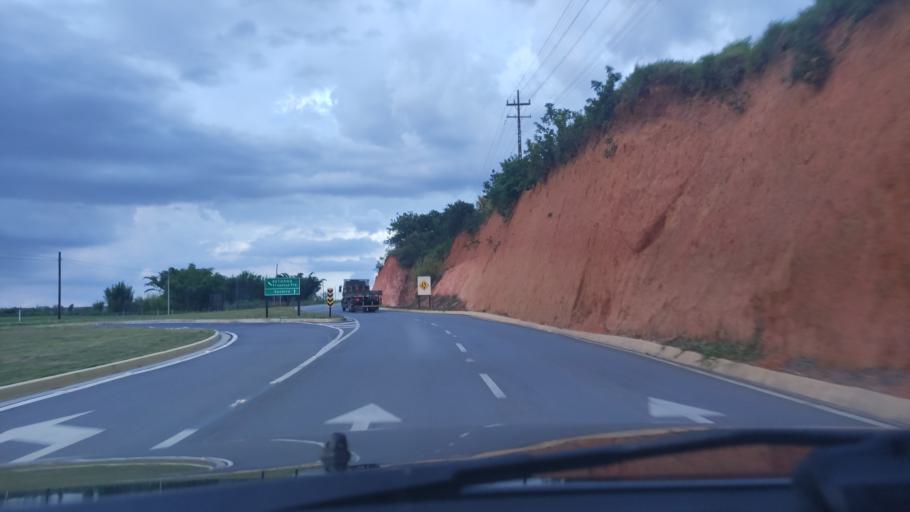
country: BR
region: Sao Paulo
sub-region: Braganca Paulista
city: Braganca Paulista
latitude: -22.8863
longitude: -46.5390
